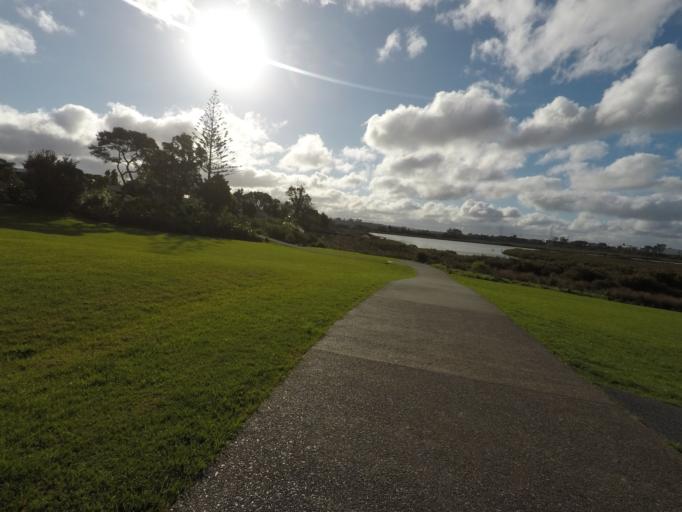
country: NZ
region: Auckland
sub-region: Auckland
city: Rosebank
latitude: -36.8910
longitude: 174.6694
